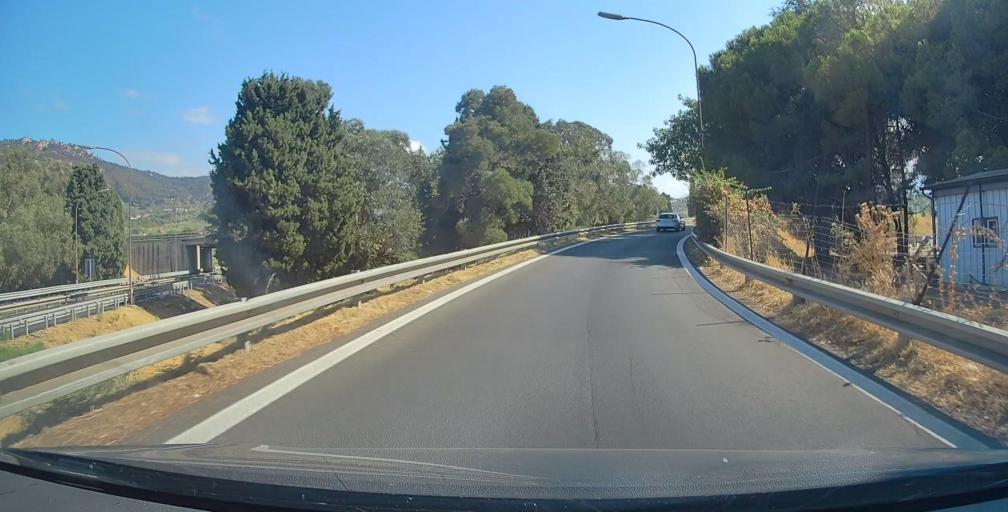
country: IT
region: Sicily
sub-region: Messina
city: Patti
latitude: 38.1442
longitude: 14.9991
